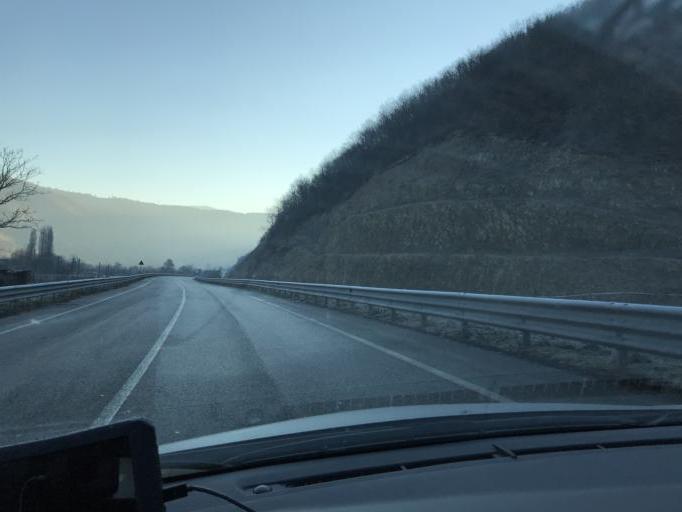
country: IT
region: Latium
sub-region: Provincia di Rieti
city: Cittaducale
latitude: 42.3539
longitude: 12.9415
